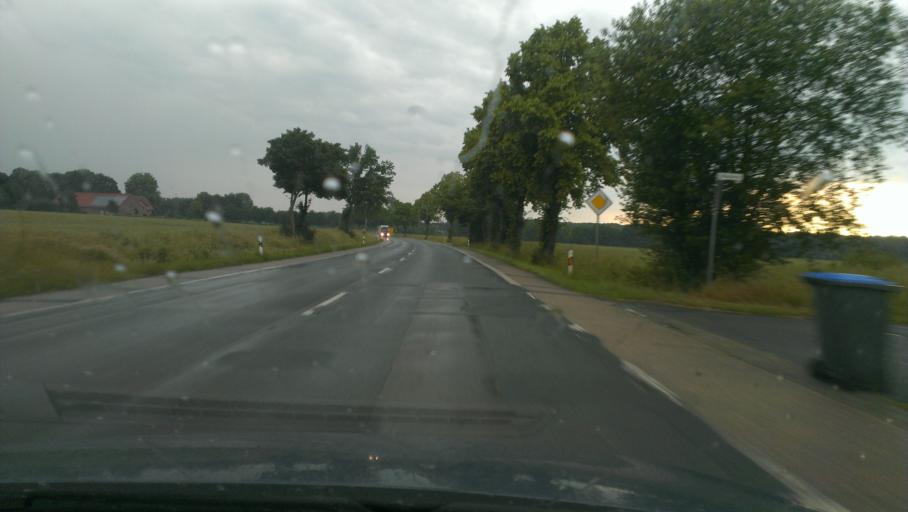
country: DE
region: North Rhine-Westphalia
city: Ahlen
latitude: 51.8164
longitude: 7.9268
